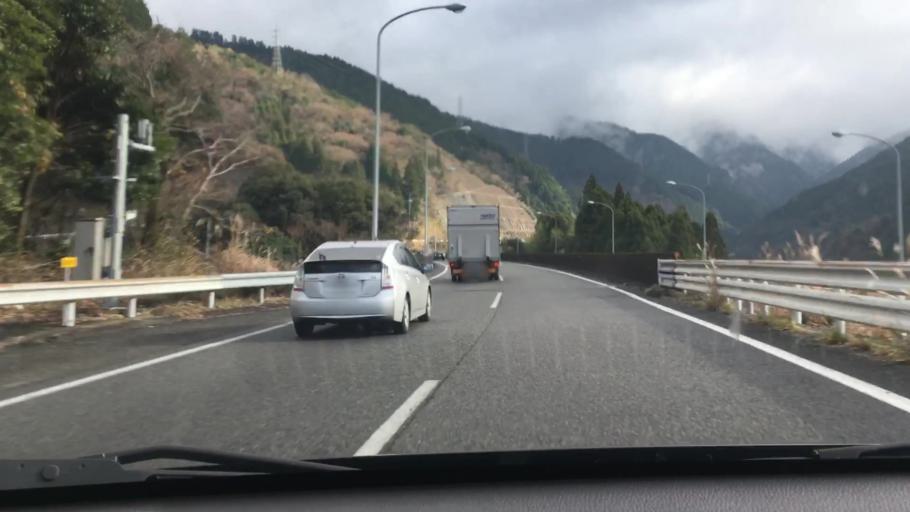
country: JP
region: Kumamoto
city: Yatsushiro
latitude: 32.4015
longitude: 130.6989
